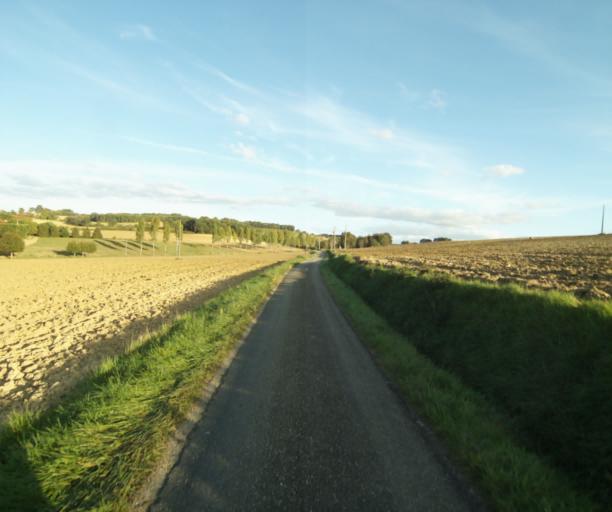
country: FR
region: Midi-Pyrenees
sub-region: Departement du Gers
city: Gondrin
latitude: 43.8805
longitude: 0.2982
